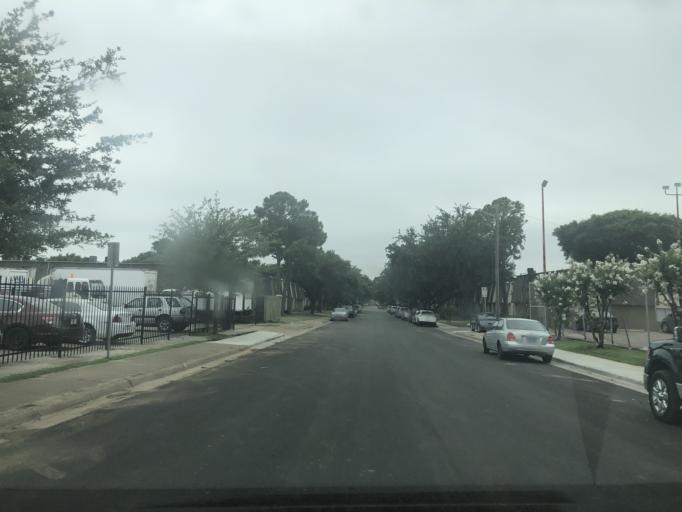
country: US
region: Texas
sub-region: Dallas County
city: University Park
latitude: 32.8597
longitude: -96.8656
